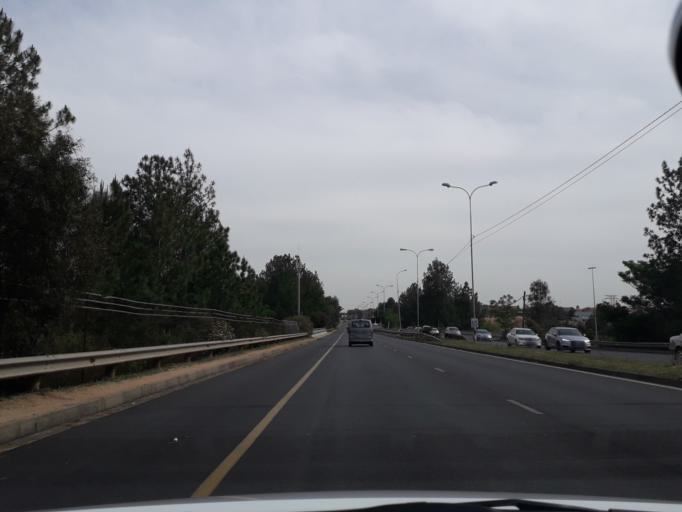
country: ZA
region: Gauteng
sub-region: City of Johannesburg Metropolitan Municipality
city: Diepsloot
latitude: -26.0337
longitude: 28.0268
